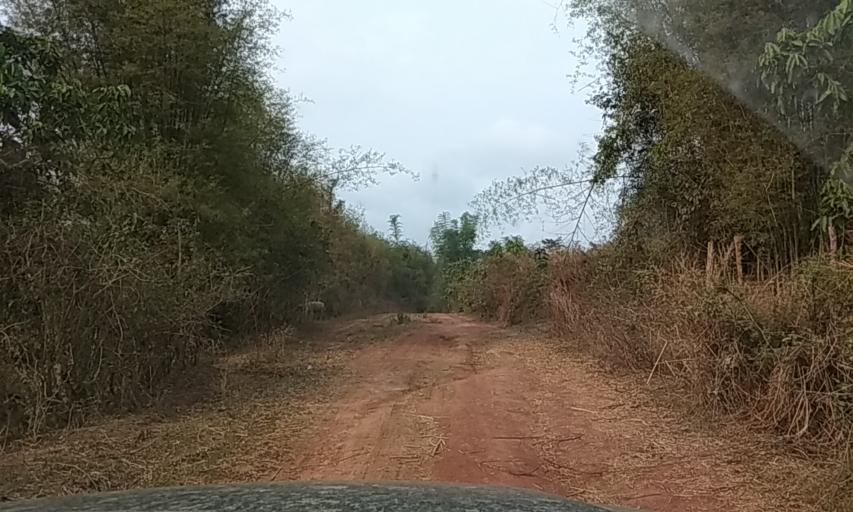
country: TH
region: Nan
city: Mae Charim
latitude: 18.4264
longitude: 101.1740
